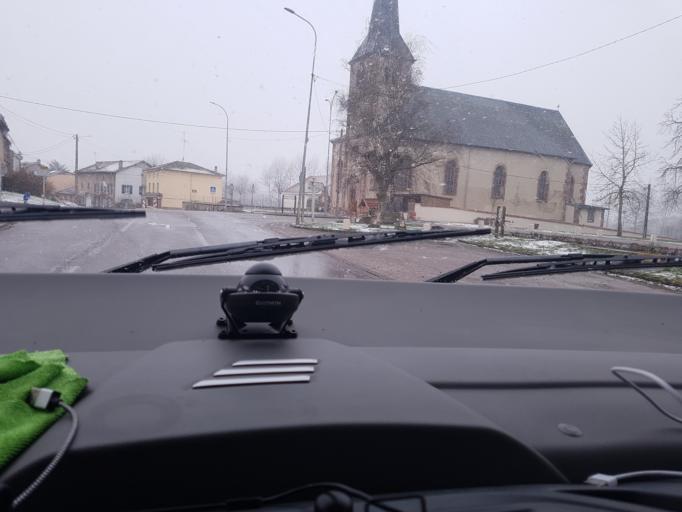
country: FR
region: Lorraine
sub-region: Departement de Meurthe-et-Moselle
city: Baccarat
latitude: 48.5613
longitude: 6.8064
